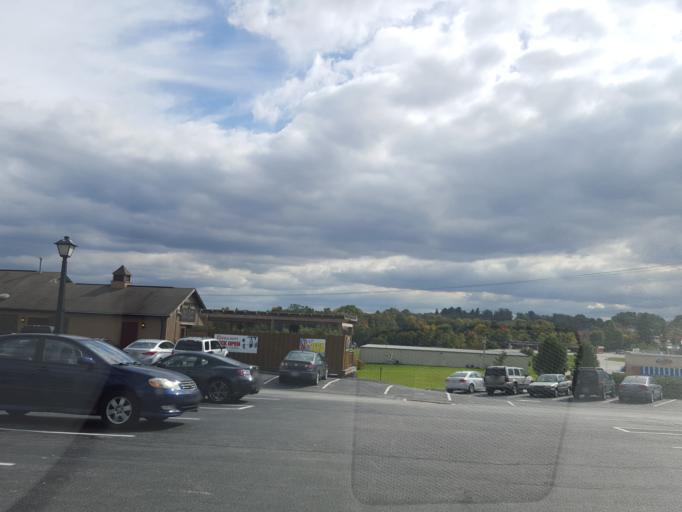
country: US
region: Pennsylvania
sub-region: York County
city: Spry
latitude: 39.9121
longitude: -76.6816
